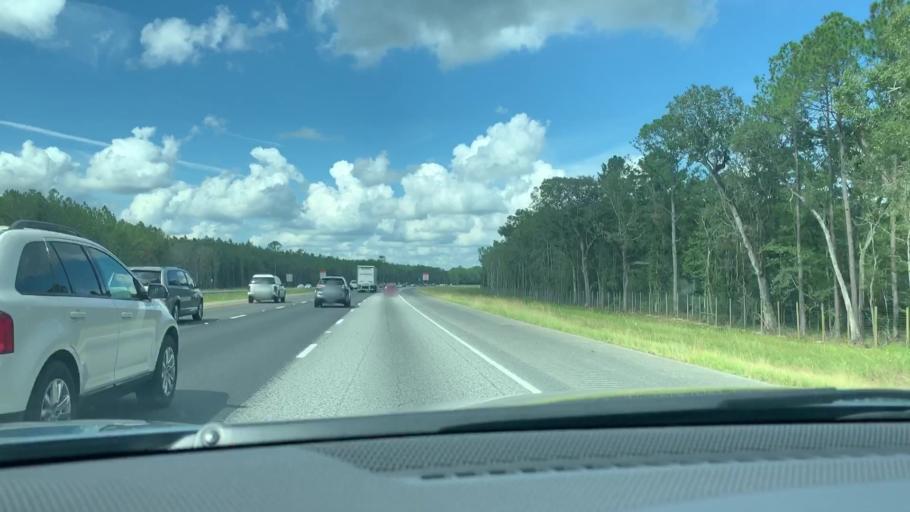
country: US
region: Georgia
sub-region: Camden County
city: Kingsland
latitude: 30.8694
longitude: -81.6829
